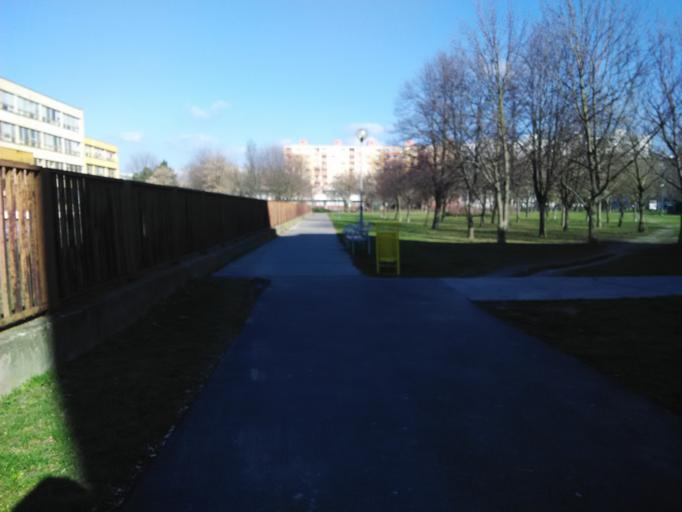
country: AT
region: Burgenland
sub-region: Politischer Bezirk Neusiedl am See
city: Kittsee
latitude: 48.1049
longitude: 17.1022
